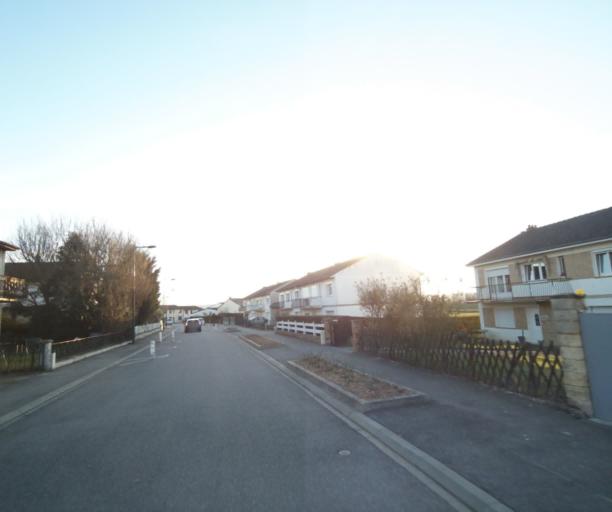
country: FR
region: Lorraine
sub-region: Departement de Meurthe-et-Moselle
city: Saulxures-les-Nancy
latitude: 48.6874
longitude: 6.2367
